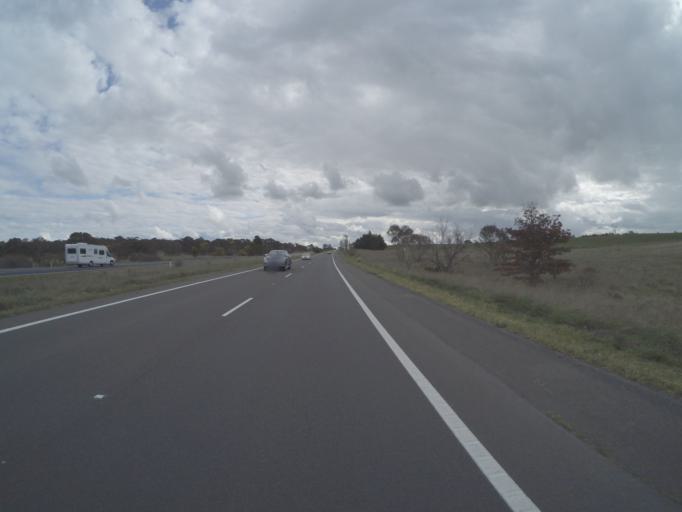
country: AU
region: New South Wales
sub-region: Goulburn Mulwaree
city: Goulburn
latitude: -34.8073
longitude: 149.6000
